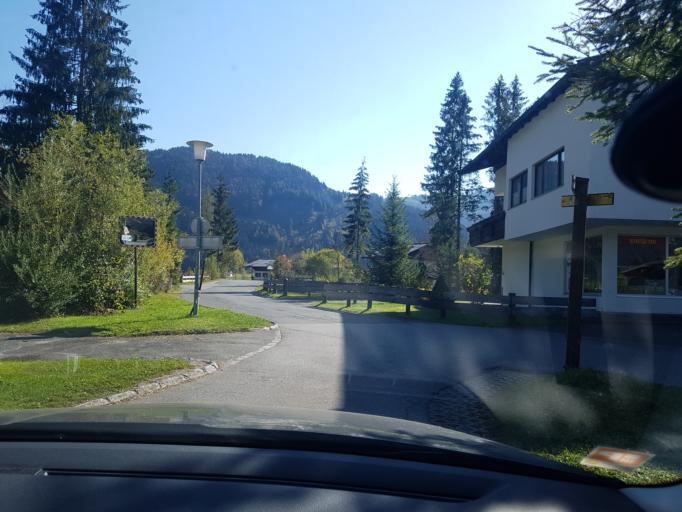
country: AT
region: Tyrol
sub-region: Politischer Bezirk Kitzbuhel
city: Fieberbrunn
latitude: 47.5125
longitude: 12.5875
